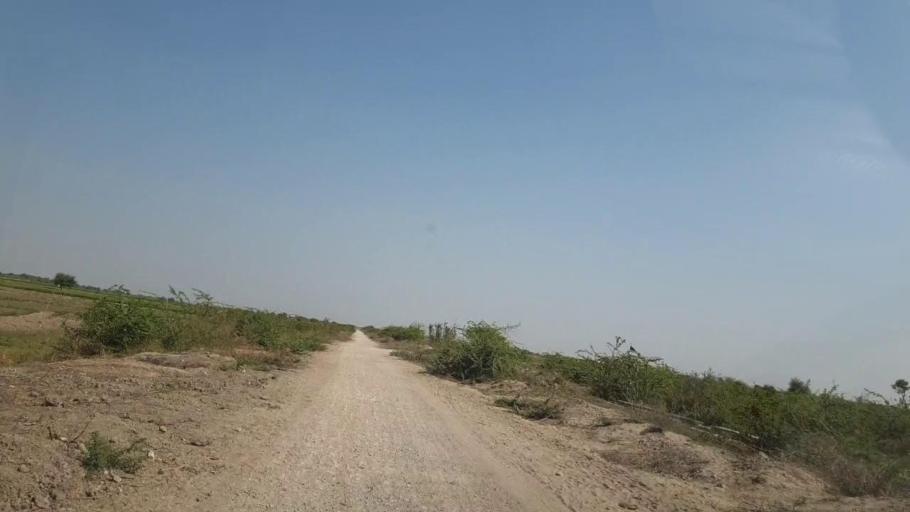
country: PK
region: Sindh
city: Nabisar
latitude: 25.0750
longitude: 69.5482
